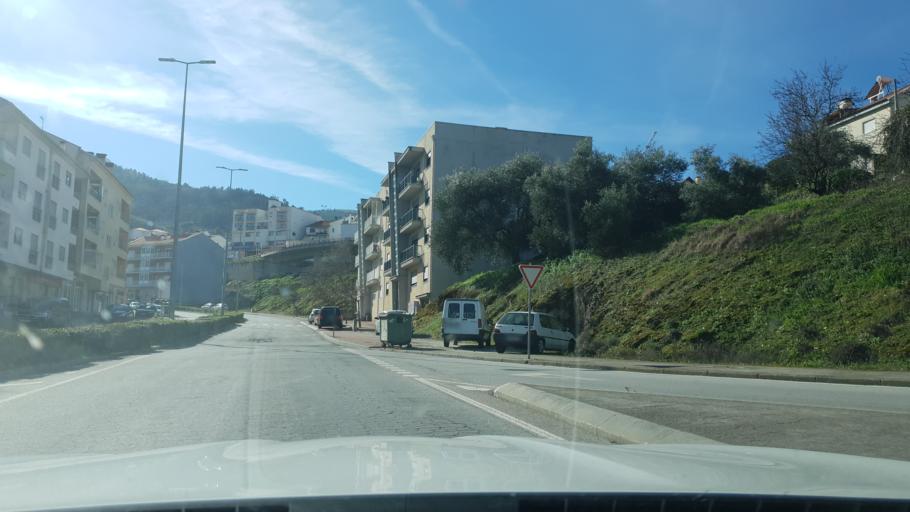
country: PT
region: Braganca
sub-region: Torre de Moncorvo
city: Torre de Moncorvo
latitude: 41.1765
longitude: -7.0502
